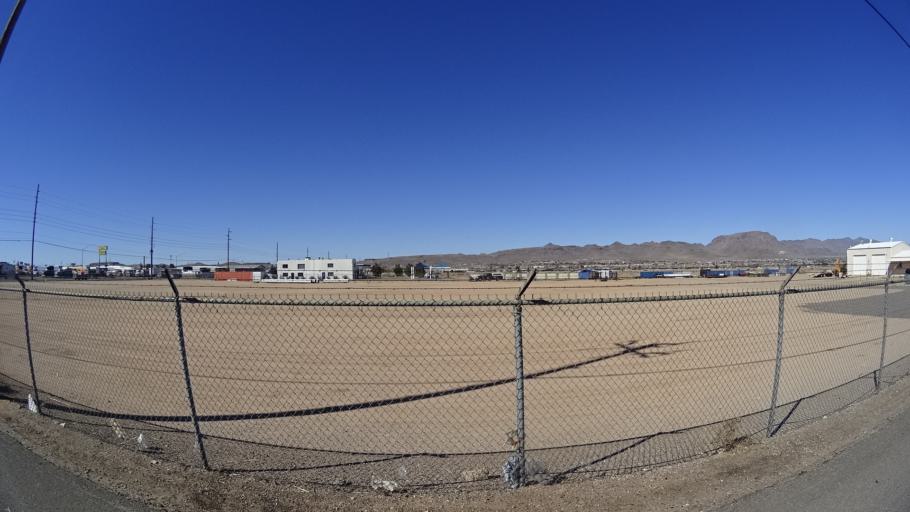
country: US
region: Arizona
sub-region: Mohave County
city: New Kingman-Butler
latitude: 35.2257
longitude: -114.0056
